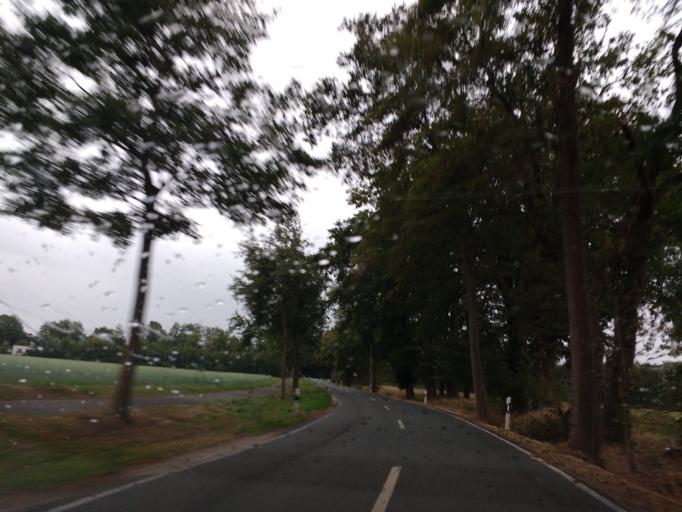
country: DE
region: North Rhine-Westphalia
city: Rietberg
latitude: 51.7355
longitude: 8.4414
